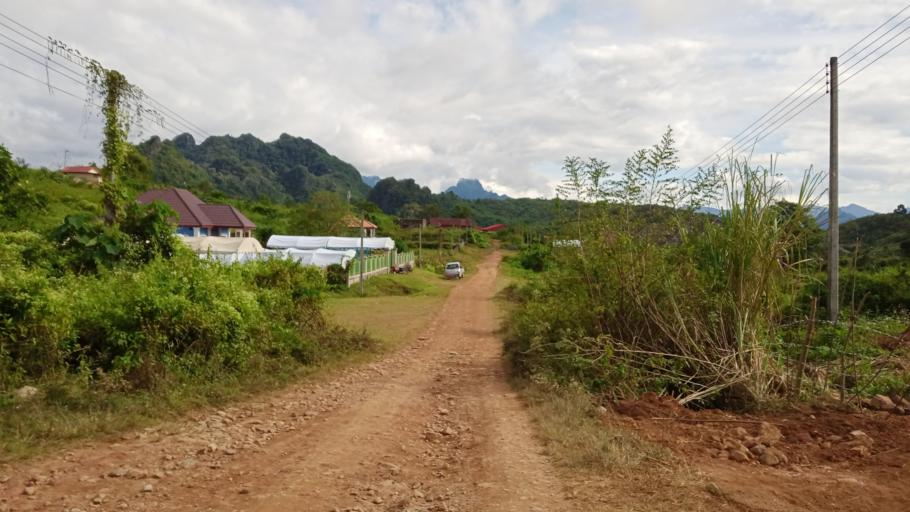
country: LA
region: Xiangkhoang
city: Phonsavan
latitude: 19.1069
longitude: 102.9276
